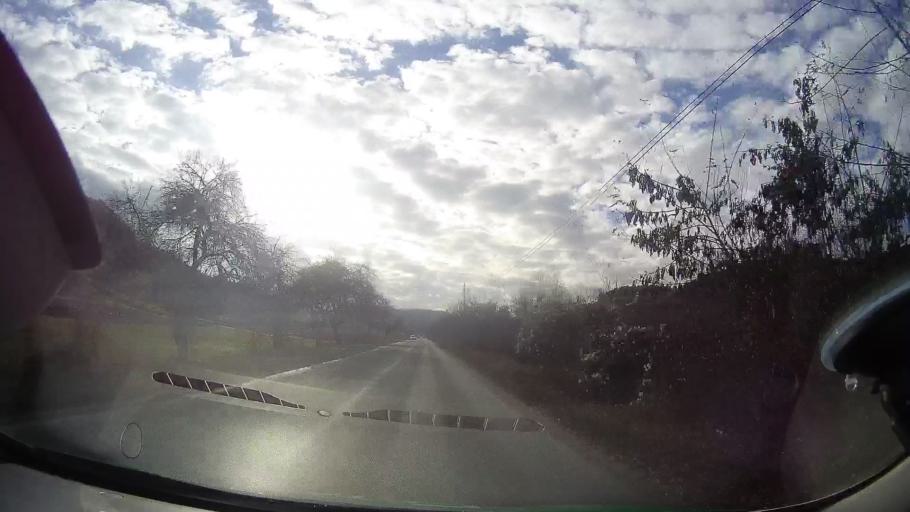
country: RO
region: Cluj
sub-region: Comuna Savadisla
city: Savadisla
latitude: 46.6832
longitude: 23.4561
